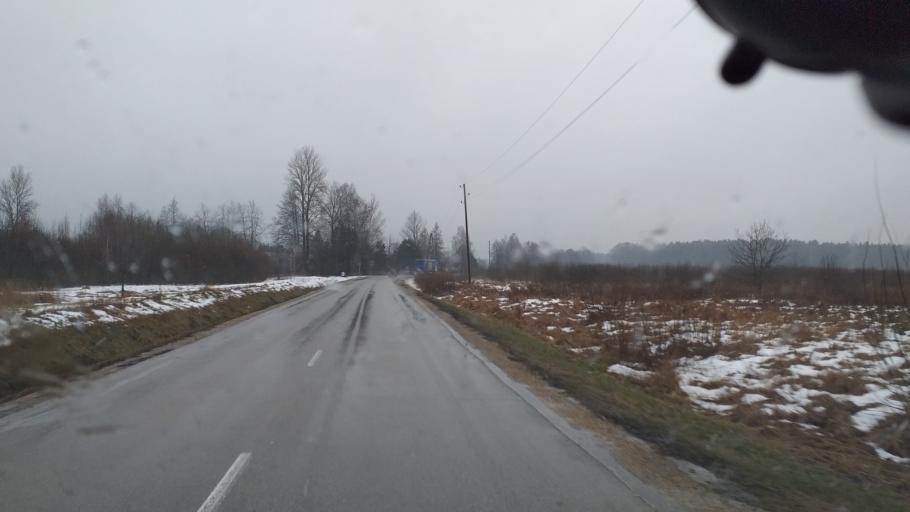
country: LV
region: Babite
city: Pinki
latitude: 56.9701
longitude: 23.9690
